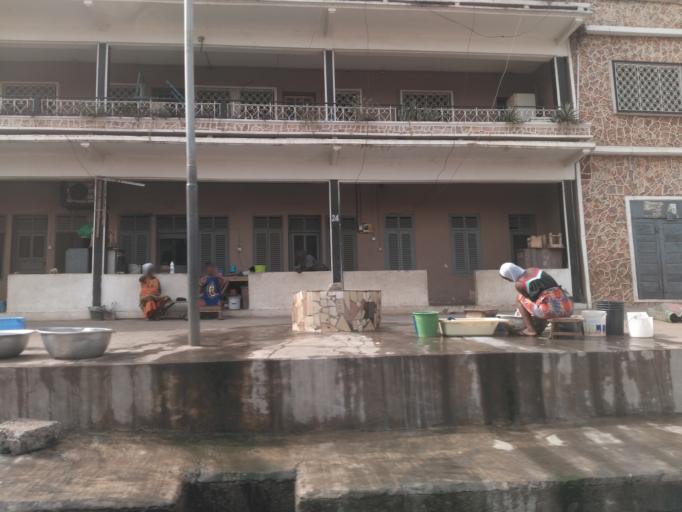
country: GH
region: Ashanti
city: Kumasi
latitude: 6.6955
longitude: -1.6114
